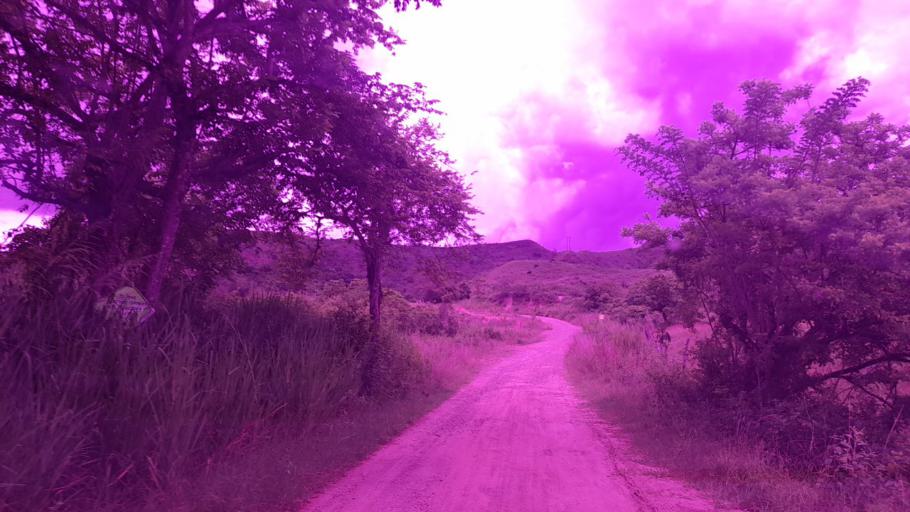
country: CO
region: Valle del Cauca
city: Andalucia
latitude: 4.1762
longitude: -76.1263
